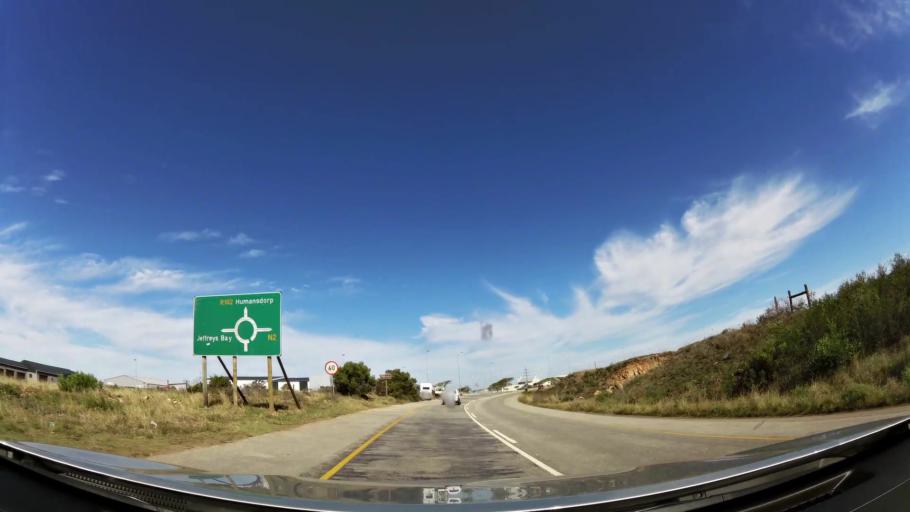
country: ZA
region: Eastern Cape
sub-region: Cacadu District Municipality
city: Jeffrey's Bay
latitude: -34.0284
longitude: 24.9019
